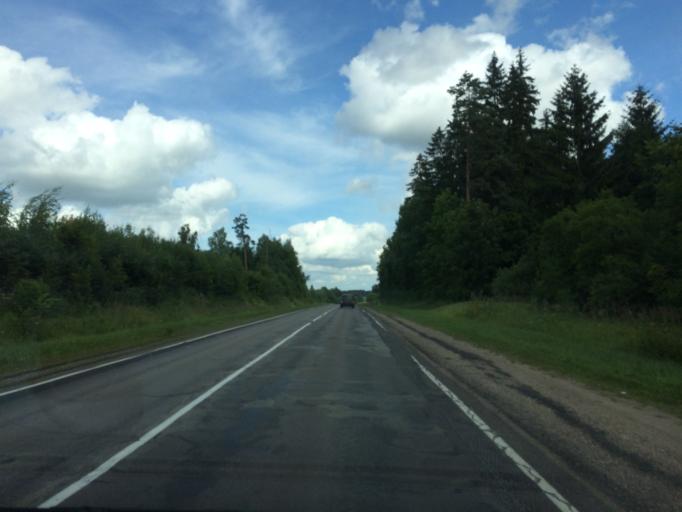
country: LV
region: Rezekne
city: Rezekne
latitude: 56.5983
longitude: 27.4215
